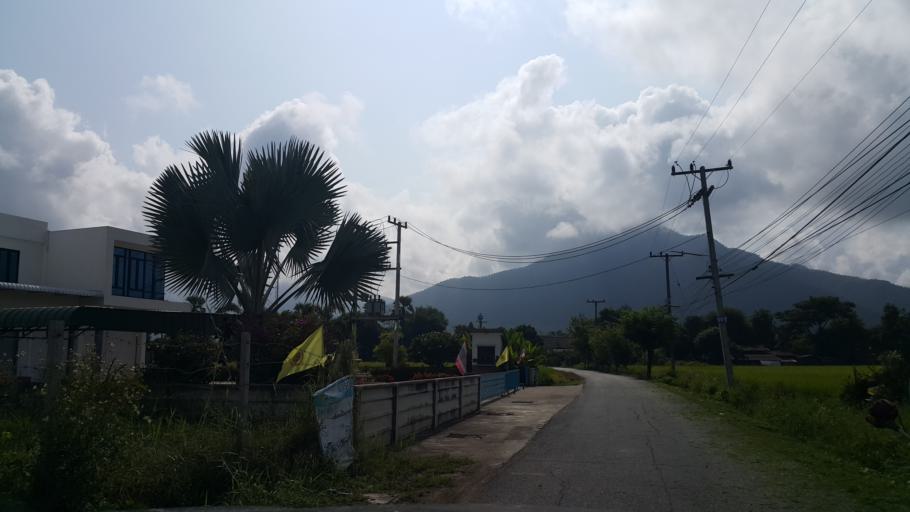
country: TH
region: Chiang Mai
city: Mae On
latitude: 18.7431
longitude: 99.2268
